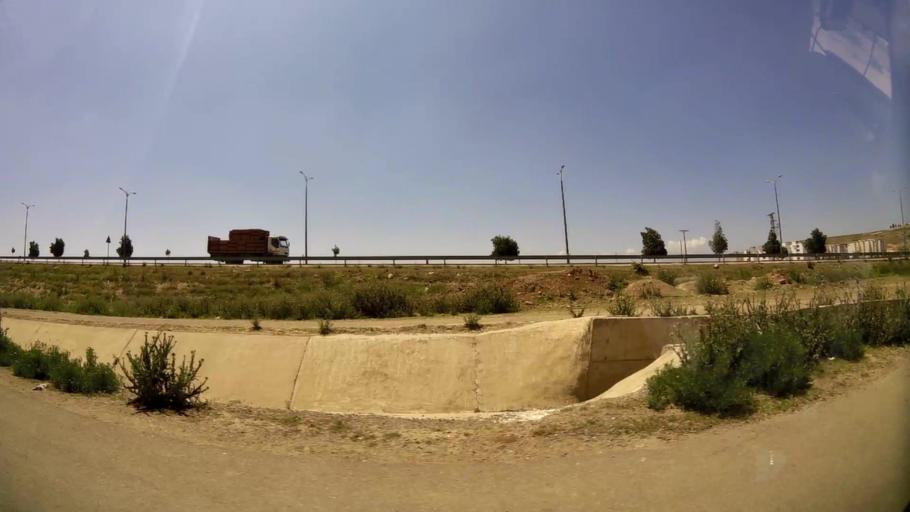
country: MA
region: Oriental
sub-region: Oujda-Angad
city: Oujda
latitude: 34.6958
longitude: -1.9411
